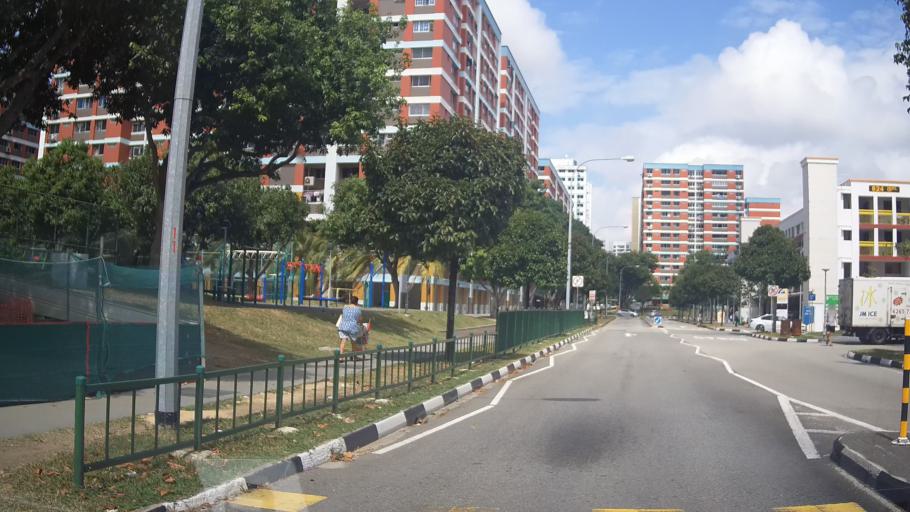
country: SG
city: Singapore
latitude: 1.3484
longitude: 103.9336
